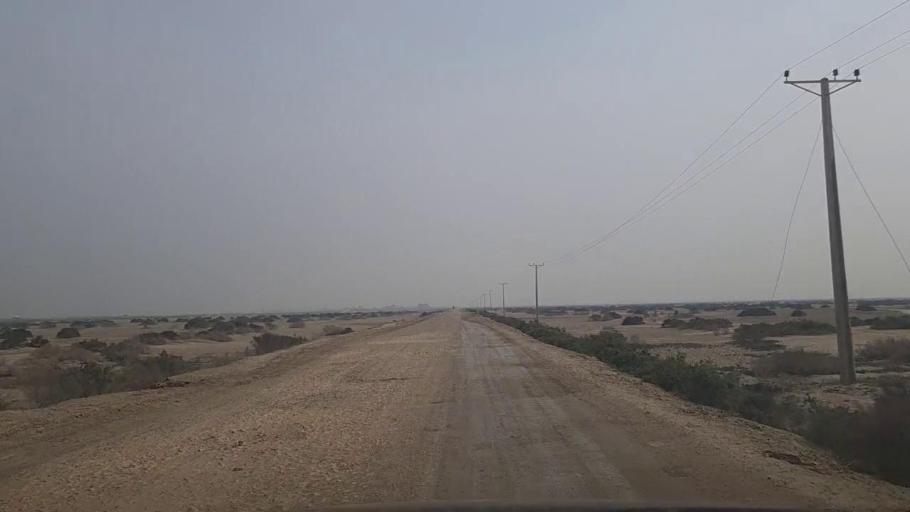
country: PK
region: Sindh
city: Mirpur Sakro
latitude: 24.4672
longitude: 67.6817
